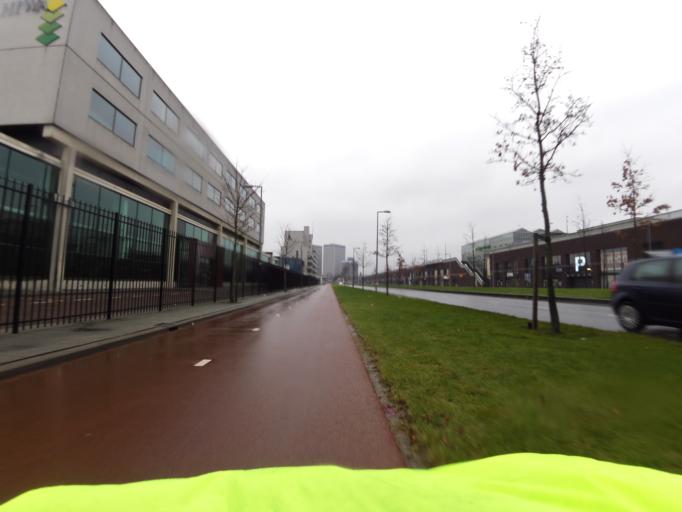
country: NL
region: South Holland
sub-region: Gemeente Rotterdam
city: Delfshaven
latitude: 51.9066
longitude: 4.4398
